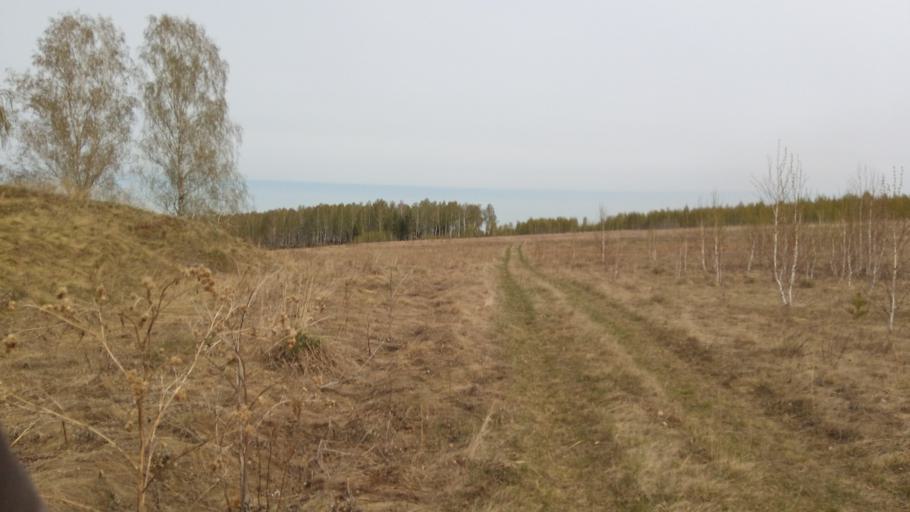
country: RU
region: Chelyabinsk
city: Timiryazevskiy
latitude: 55.0123
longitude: 60.8619
